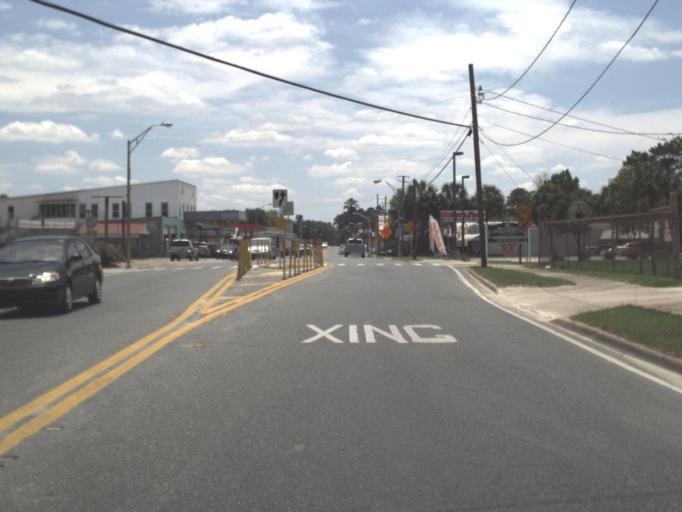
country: US
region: Florida
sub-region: Calhoun County
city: Blountstown
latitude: 30.4464
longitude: -85.0458
